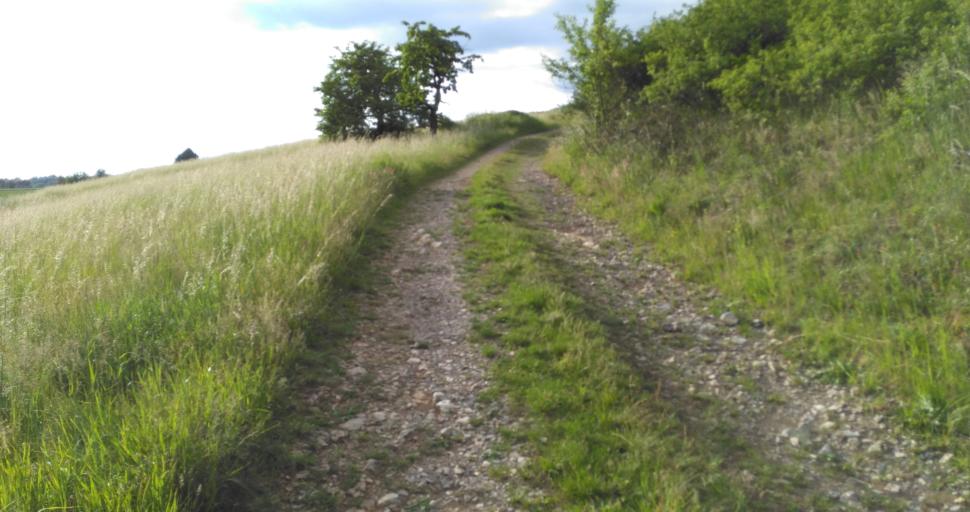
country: CZ
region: Central Bohemia
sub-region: Okres Beroun
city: Beroun
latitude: 49.9215
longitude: 14.1312
